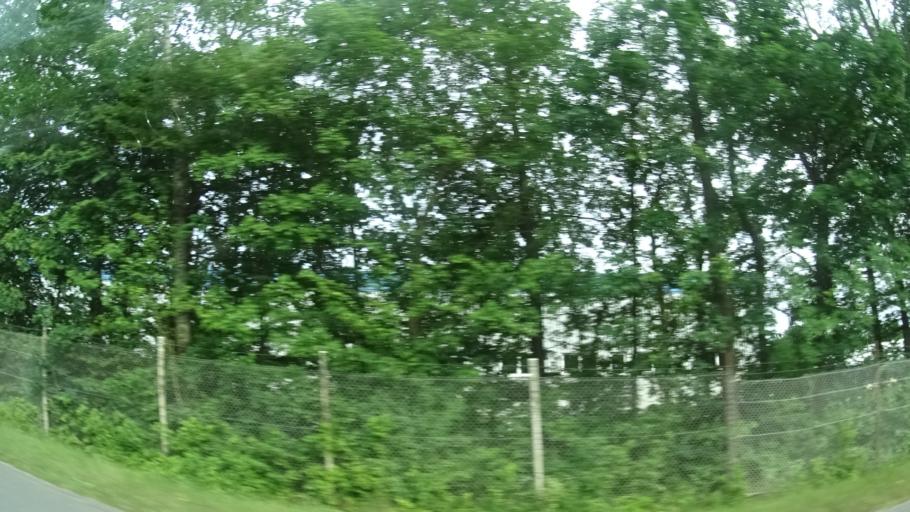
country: DE
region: North Rhine-Westphalia
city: Warburg
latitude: 51.5062
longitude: 9.1328
